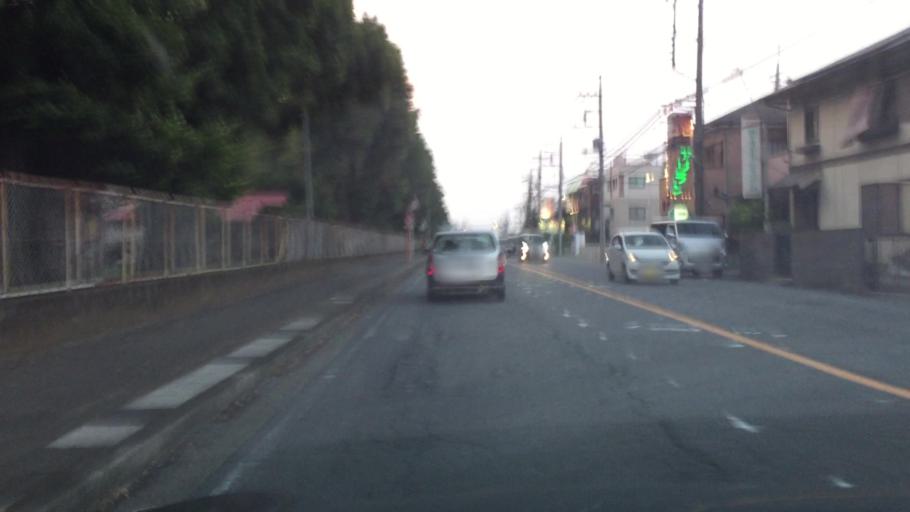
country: JP
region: Saitama
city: Yono
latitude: 35.9165
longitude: 139.6051
